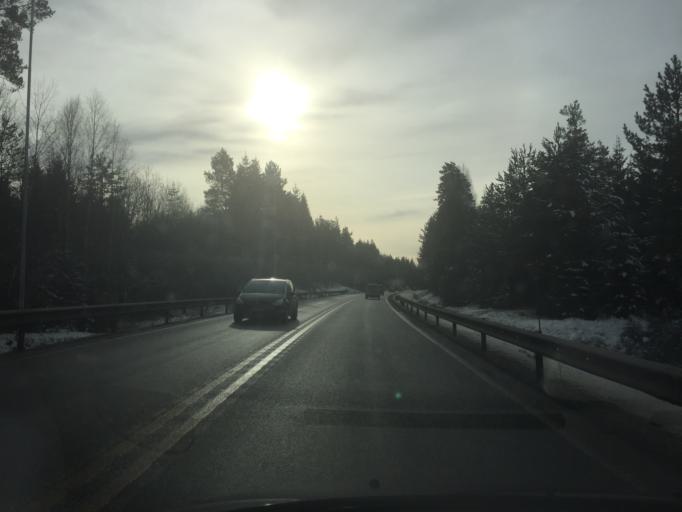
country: NO
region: Hedmark
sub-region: Stange
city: Stange
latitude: 60.7245
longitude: 11.2913
